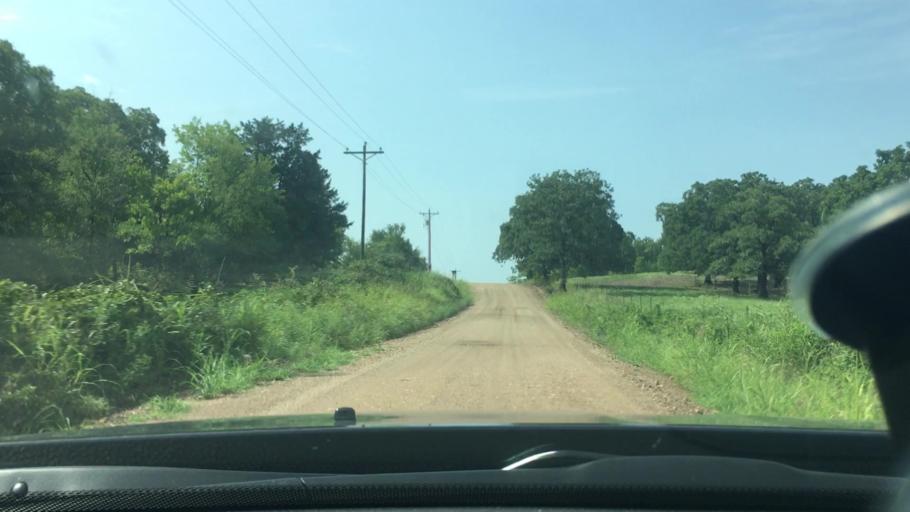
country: US
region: Oklahoma
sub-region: Atoka County
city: Atoka
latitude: 34.4558
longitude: -96.0407
